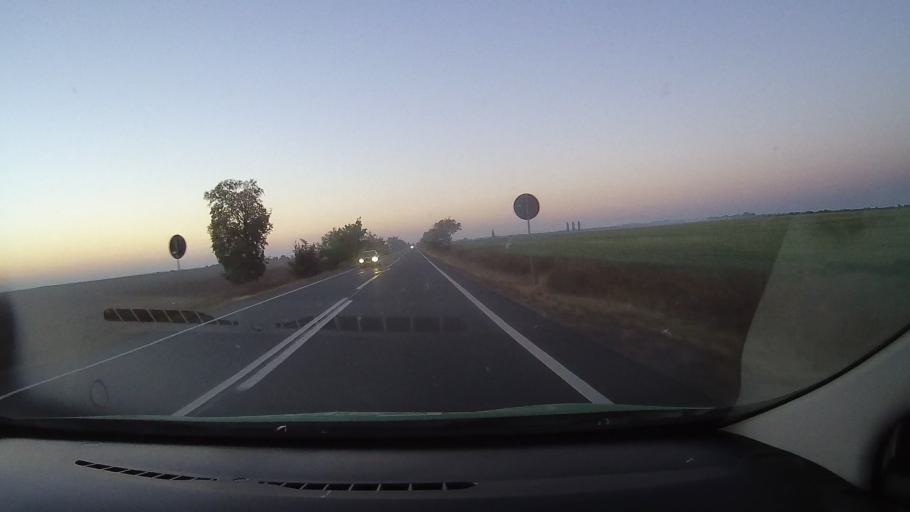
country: RO
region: Bihor
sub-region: Comuna Tarcea
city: Tarcea
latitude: 47.4809
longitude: 22.1626
